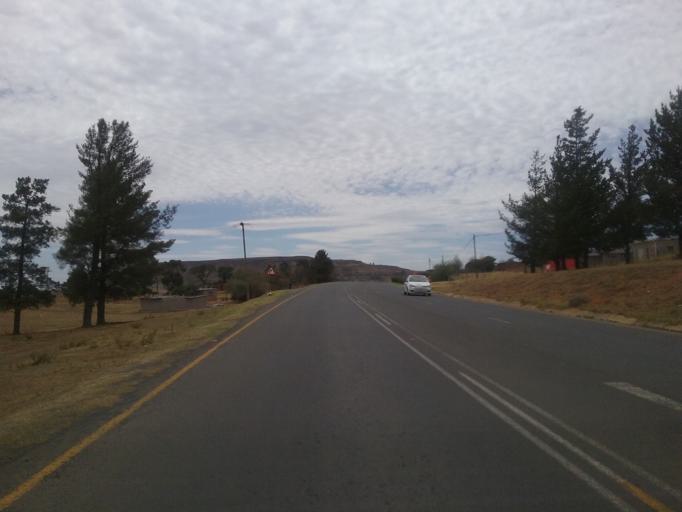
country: LS
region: Maseru
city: Nako
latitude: -29.6282
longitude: 27.4864
